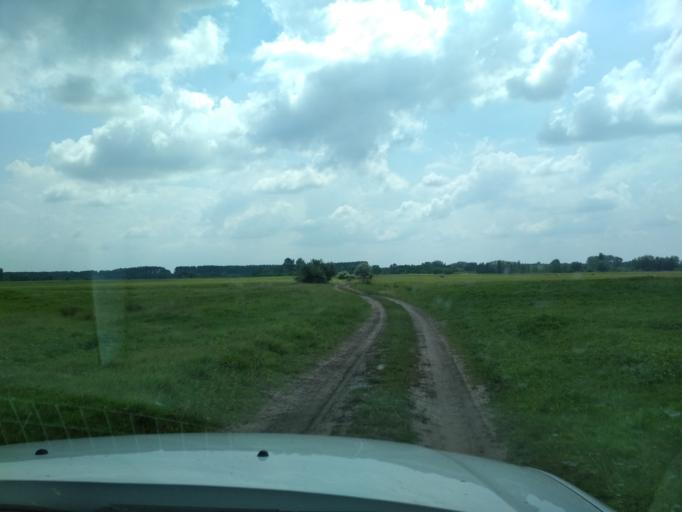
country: HU
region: Pest
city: Tapioszentmarton
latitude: 47.3728
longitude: 19.7508
